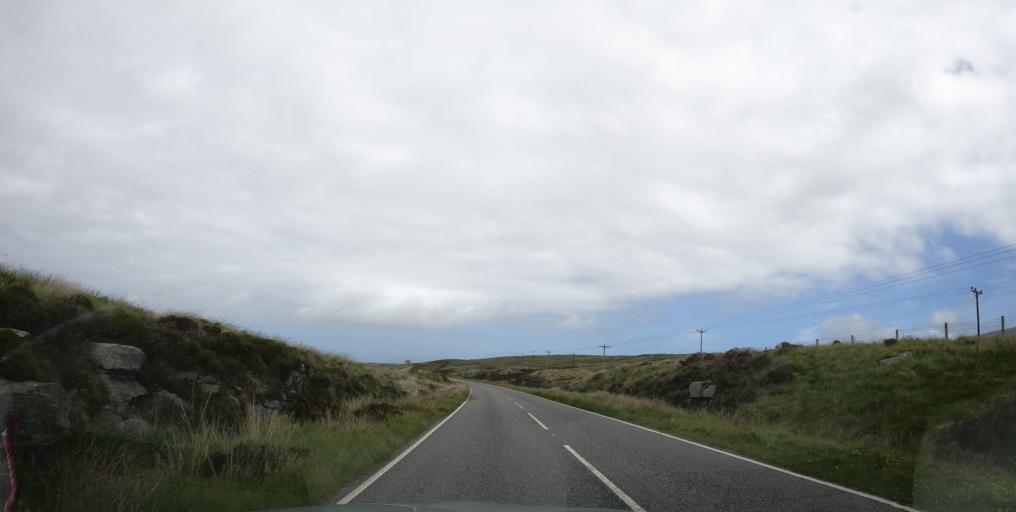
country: GB
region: Scotland
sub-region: Eilean Siar
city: Isle of South Uist
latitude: 57.2632
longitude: -7.3693
